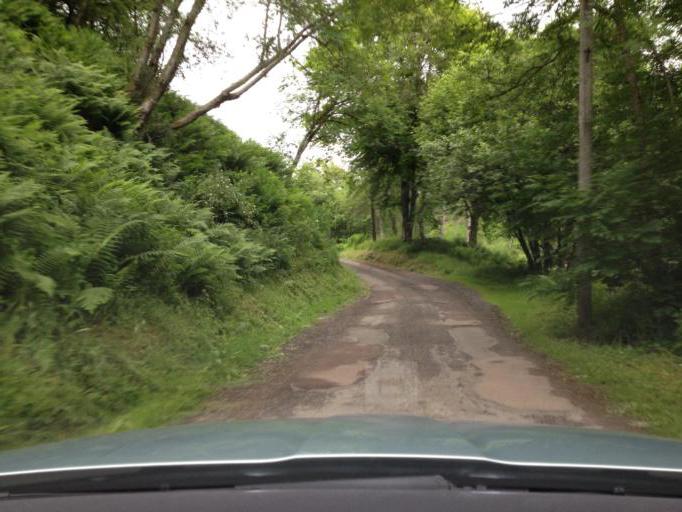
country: GB
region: Scotland
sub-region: Aberdeenshire
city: Aboyne
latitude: 56.8997
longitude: -2.7566
